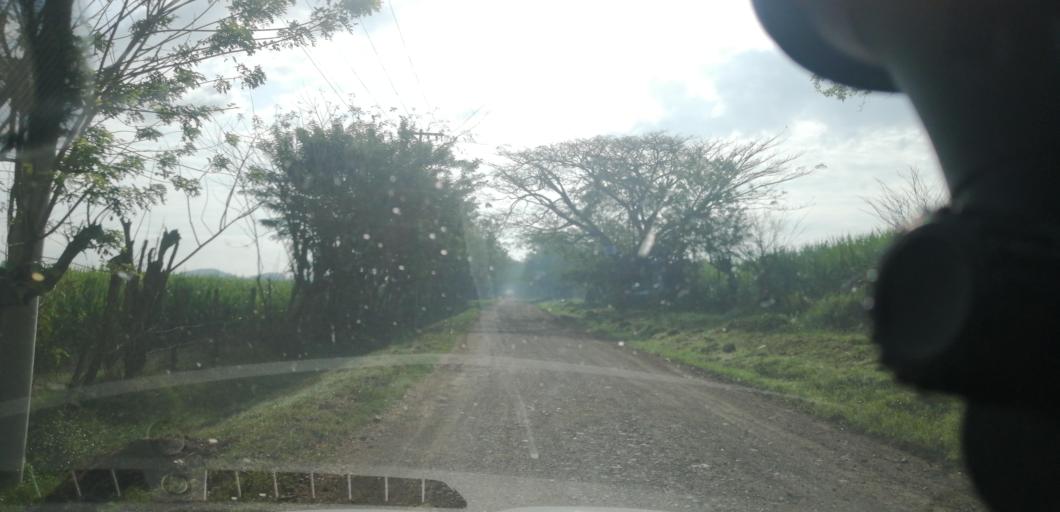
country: CO
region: Valle del Cauca
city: Yumbo
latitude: 3.5838
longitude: -76.4257
